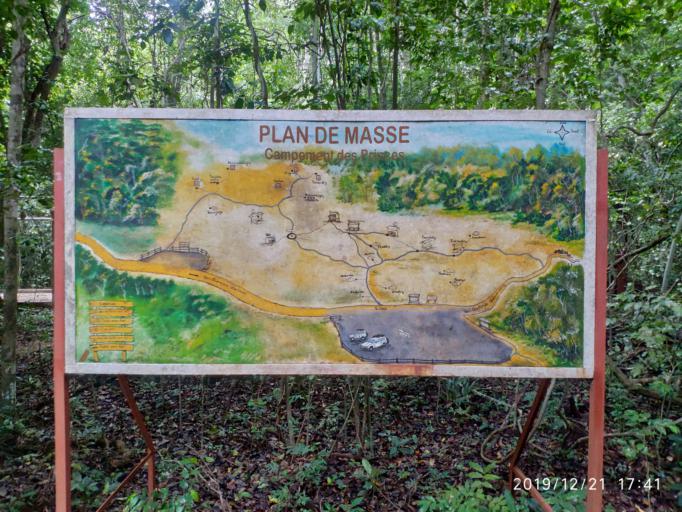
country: MG
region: Diana
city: Ambilobe
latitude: -12.9587
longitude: 49.1198
